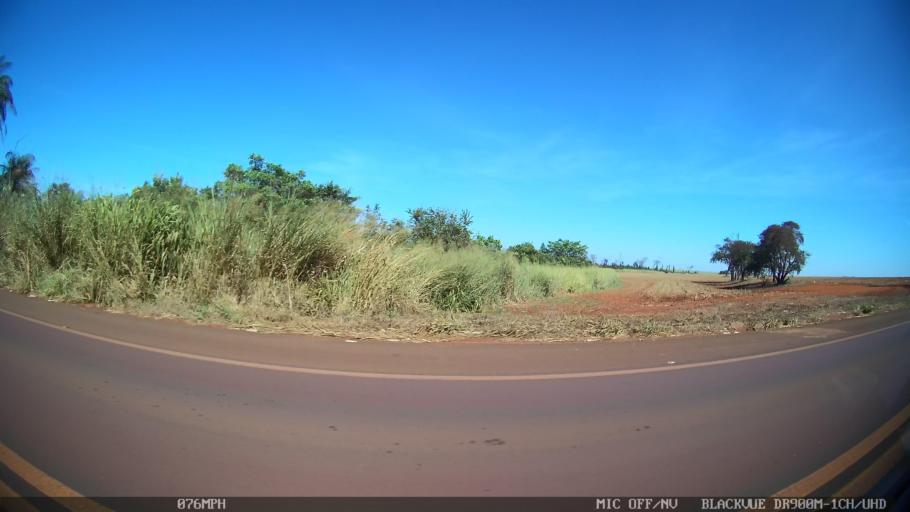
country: BR
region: Sao Paulo
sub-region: Guaira
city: Guaira
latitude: -20.4458
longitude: -48.4126
